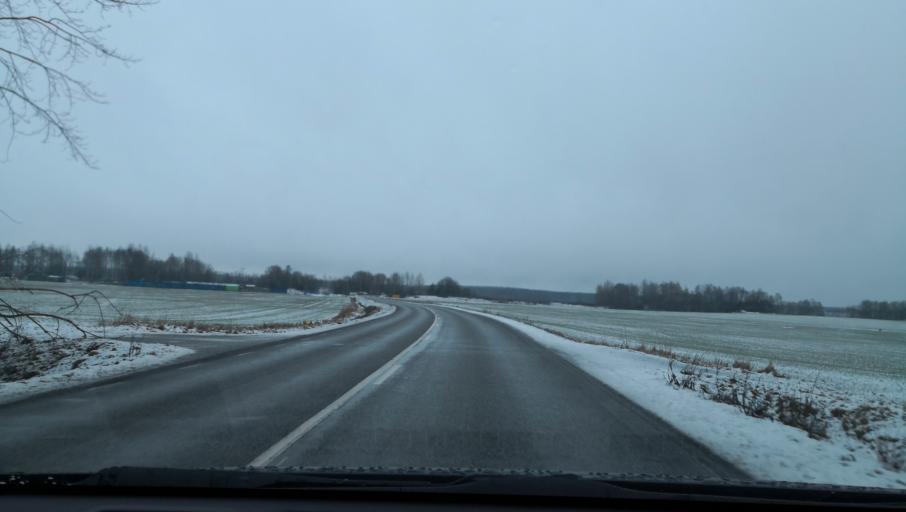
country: SE
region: Vaestmanland
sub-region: Kopings Kommun
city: Koping
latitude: 59.5243
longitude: 15.9506
